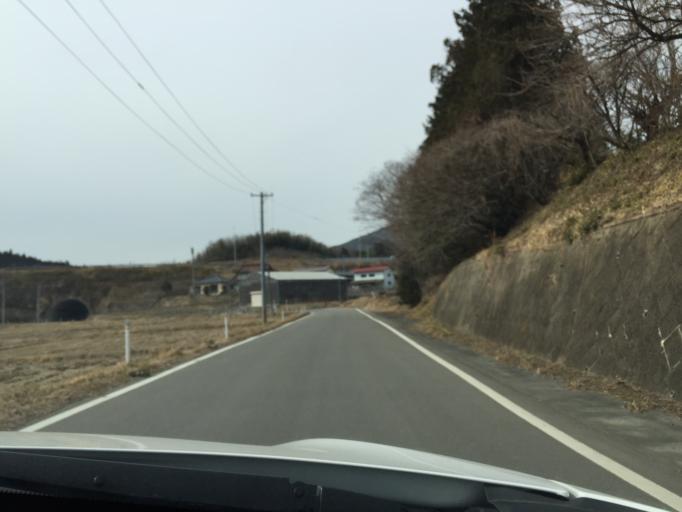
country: JP
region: Fukushima
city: Ishikawa
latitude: 37.2439
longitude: 140.5604
